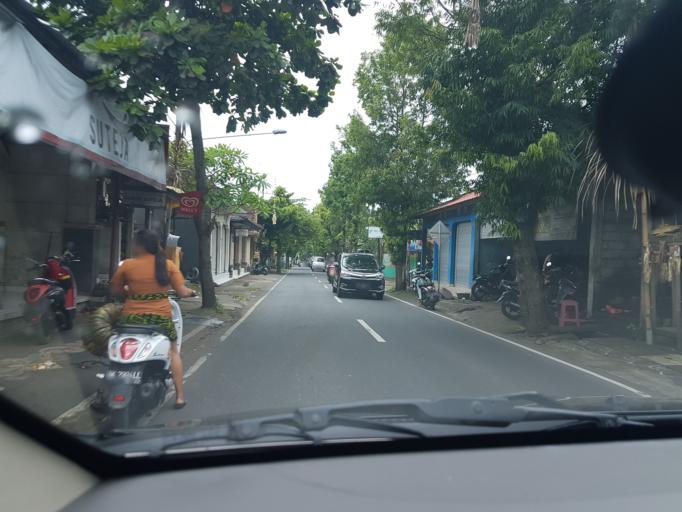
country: ID
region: Bali
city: Banjar Pande
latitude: -8.5041
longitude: 115.2432
